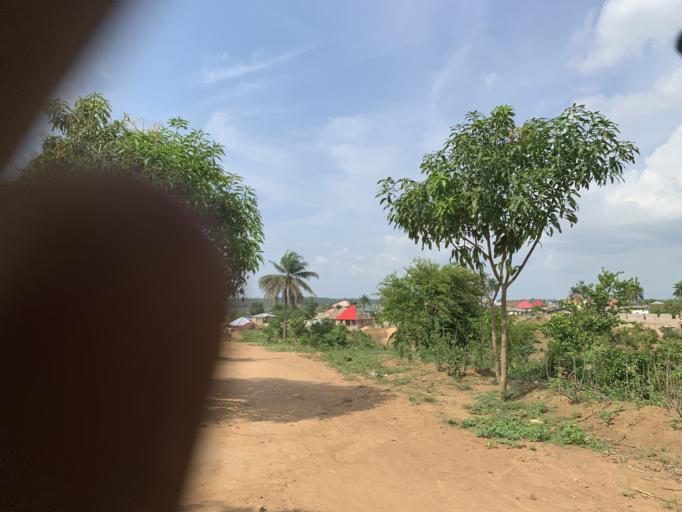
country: SL
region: Western Area
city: Waterloo
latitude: 8.3491
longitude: -13.0409
